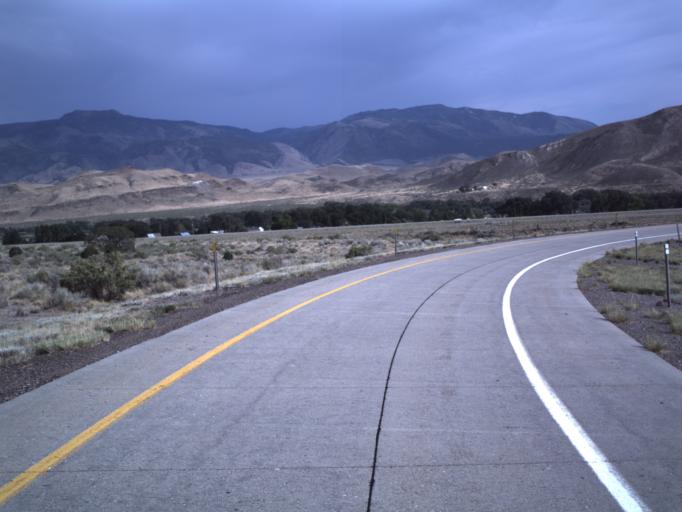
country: US
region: Utah
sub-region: Sevier County
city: Monroe
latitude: 38.6023
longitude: -112.2523
